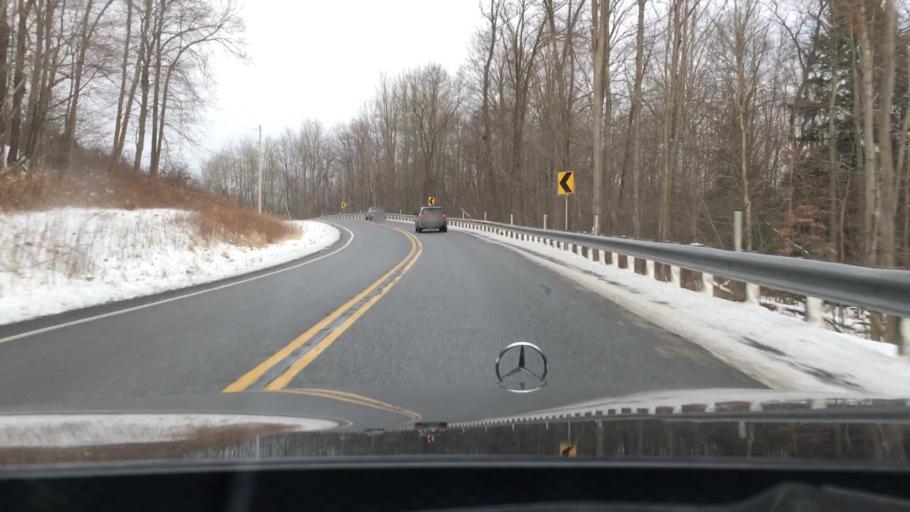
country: US
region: Pennsylvania
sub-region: Cambria County
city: Gallitzin
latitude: 40.5161
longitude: -78.5795
